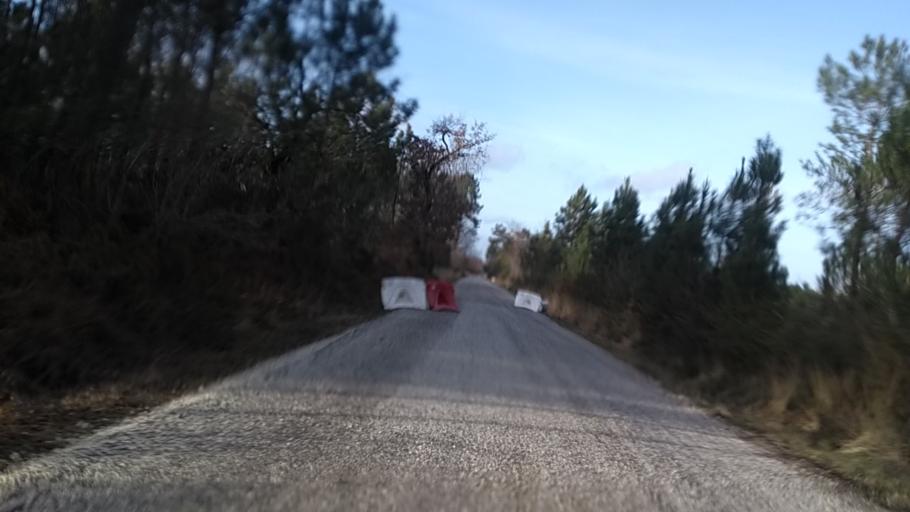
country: FR
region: Aquitaine
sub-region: Departement de la Gironde
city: Le Barp
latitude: 44.5869
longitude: -0.7695
